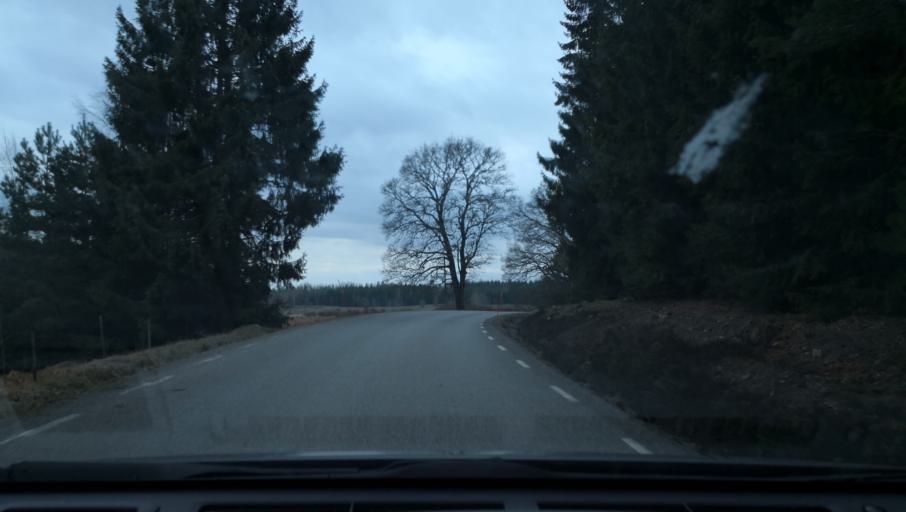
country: SE
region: Vaestmanland
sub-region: Kopings Kommun
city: Kolsva
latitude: 59.5681
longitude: 15.7711
